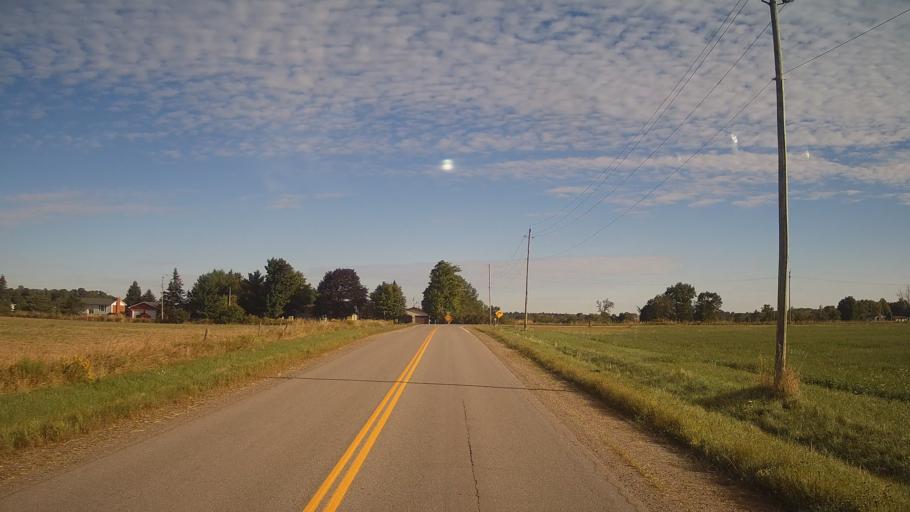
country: CA
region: Ontario
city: Gananoque
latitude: 44.3771
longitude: -76.1401
